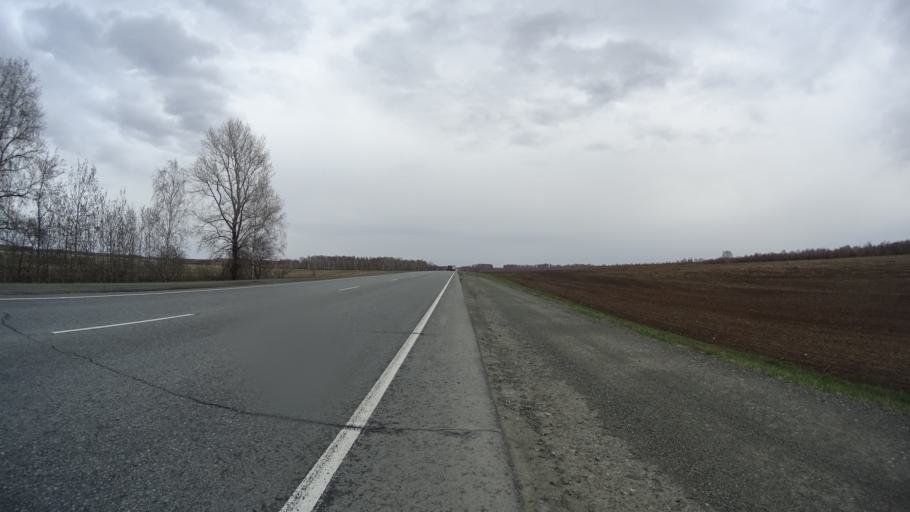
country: RU
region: Chelyabinsk
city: Krasnogorskiy
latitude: 54.6648
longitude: 61.2531
